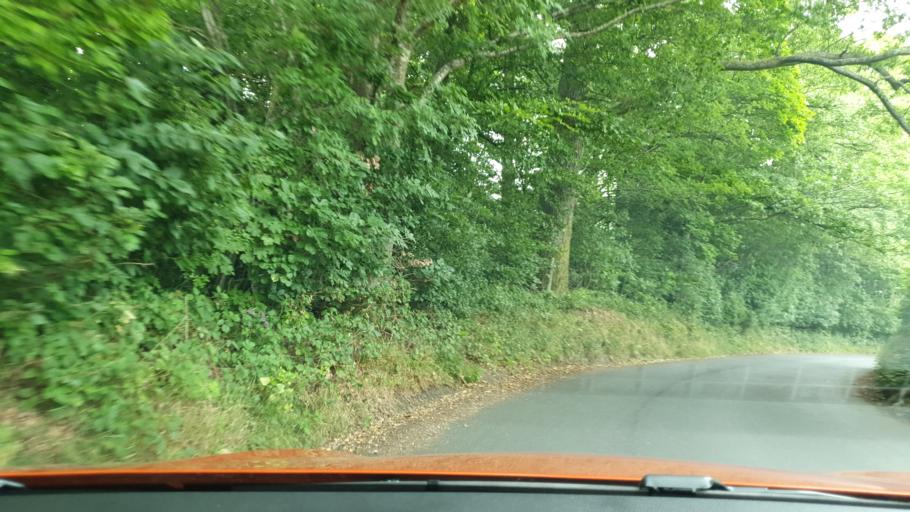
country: GB
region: England
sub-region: Cumbria
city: Penrith
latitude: 54.5912
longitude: -2.8420
